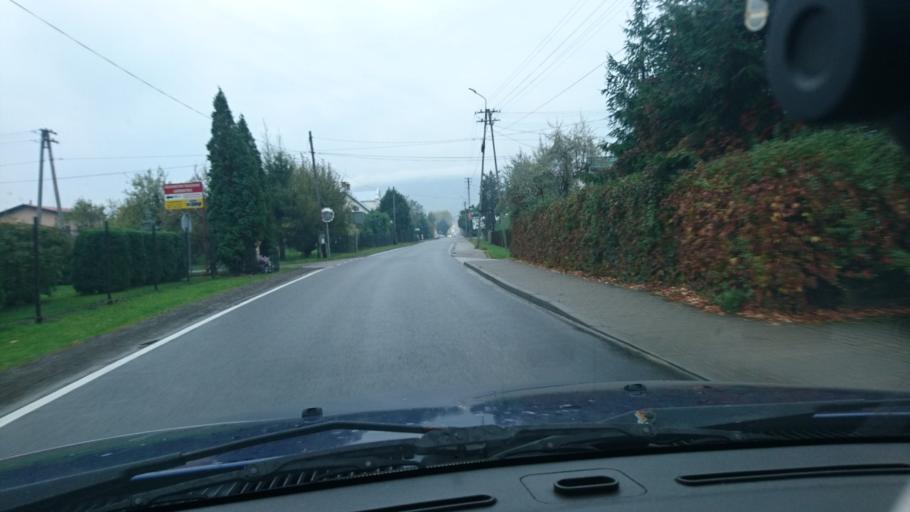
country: PL
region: Silesian Voivodeship
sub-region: Powiat bielski
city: Kozy
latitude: 49.8530
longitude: 19.1409
